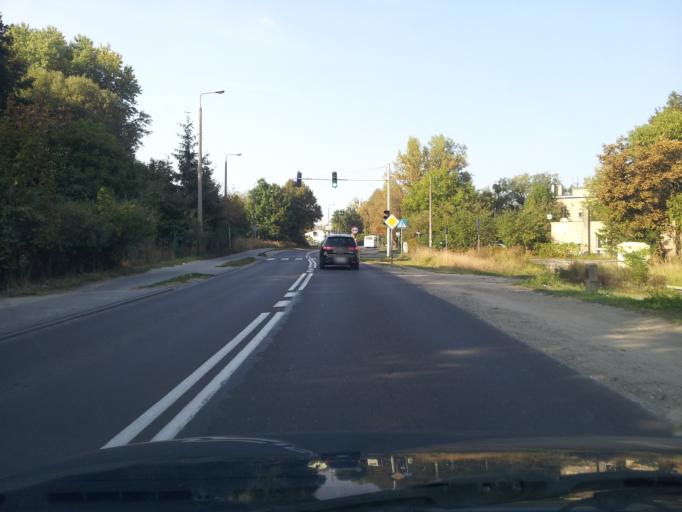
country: PL
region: Kujawsko-Pomorskie
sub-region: Powiat torunski
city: Lubicz Dolny
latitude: 53.0450
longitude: 18.7010
